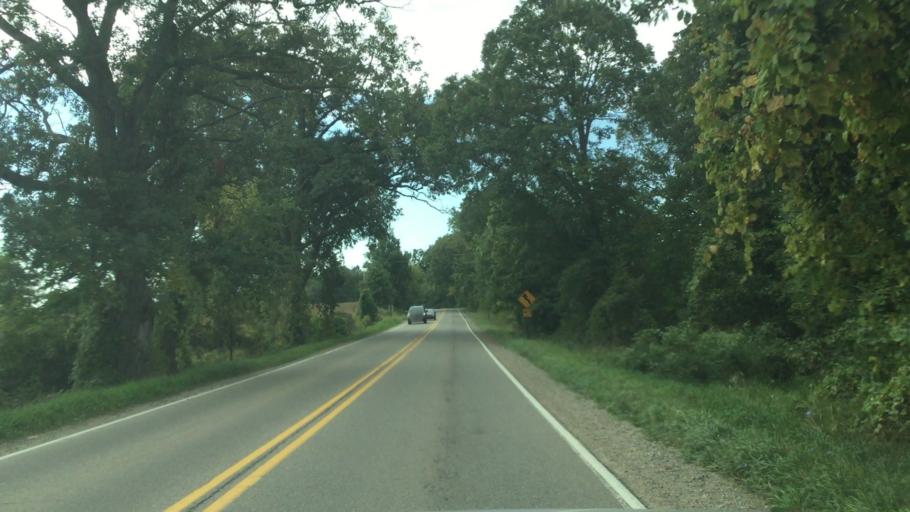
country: US
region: Michigan
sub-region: Genesee County
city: Argentine
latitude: 42.7008
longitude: -83.8404
